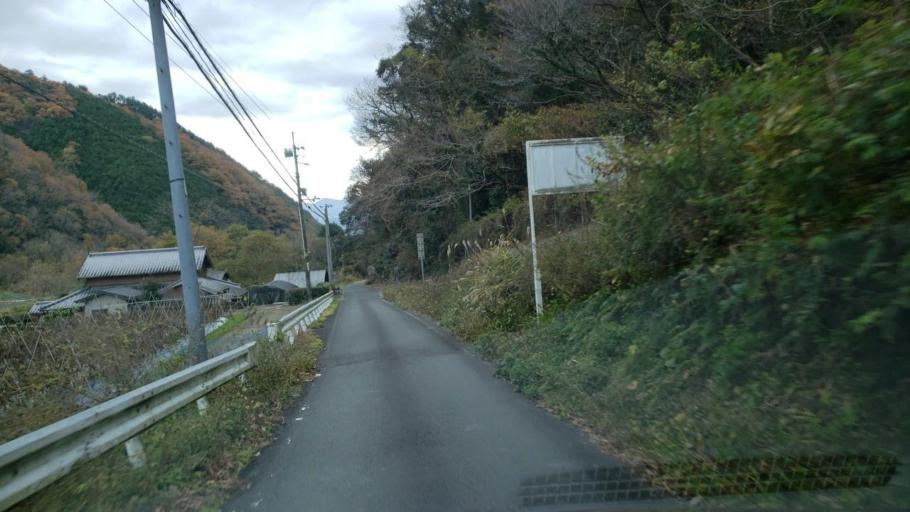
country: JP
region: Tokushima
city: Wakimachi
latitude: 34.1163
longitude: 134.2253
